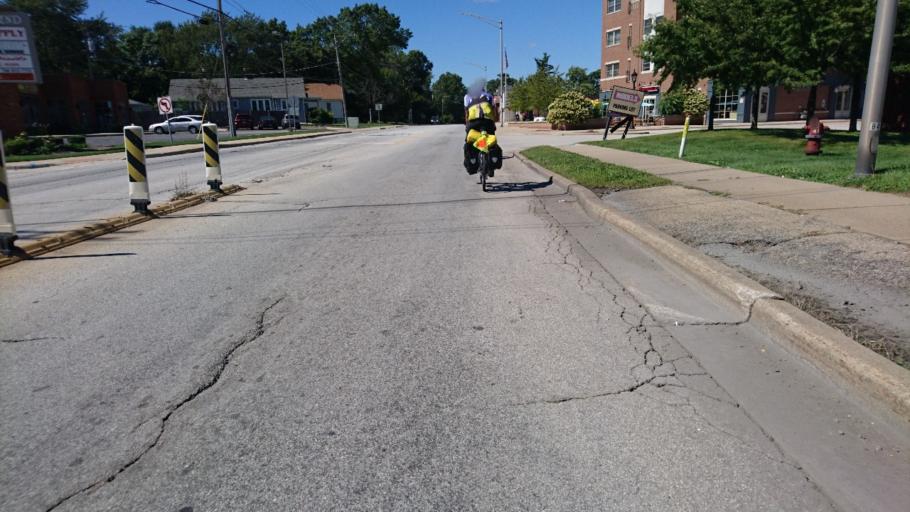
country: US
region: Illinois
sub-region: Cook County
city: Glenwood
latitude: 41.5438
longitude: -87.6121
